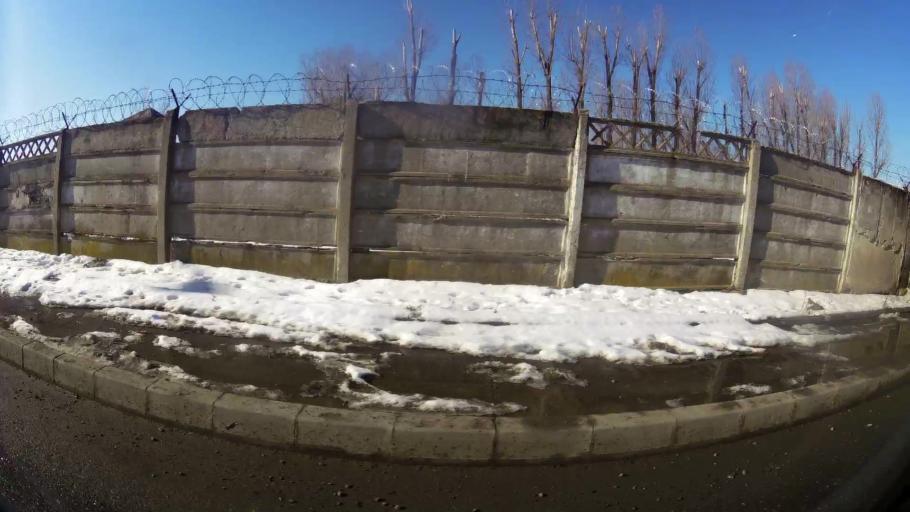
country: RO
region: Ilfov
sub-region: Comuna Magurele
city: Magurele
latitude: 44.3912
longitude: 26.0538
